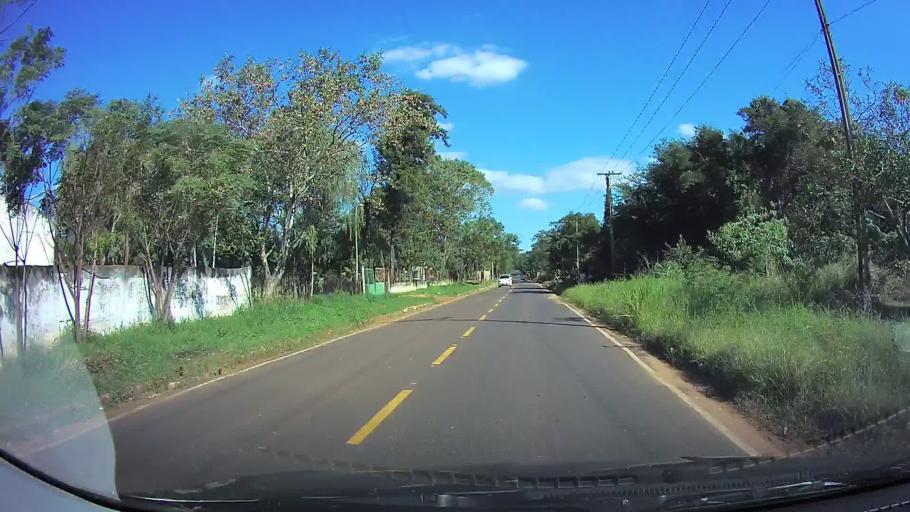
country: PY
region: Central
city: Limpio
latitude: -25.1948
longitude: -57.4769
